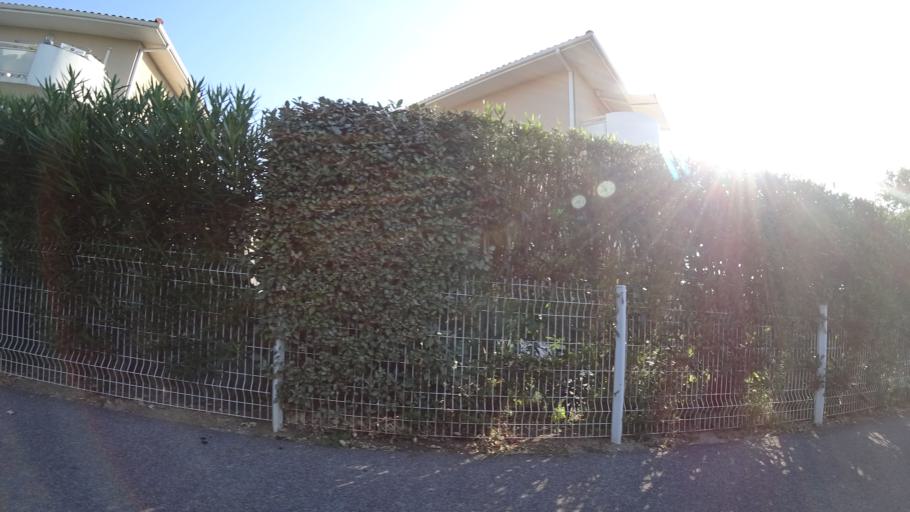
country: FR
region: Languedoc-Roussillon
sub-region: Departement des Pyrenees-Orientales
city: Sainte-Marie-Plage
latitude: 42.7280
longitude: 3.0195
